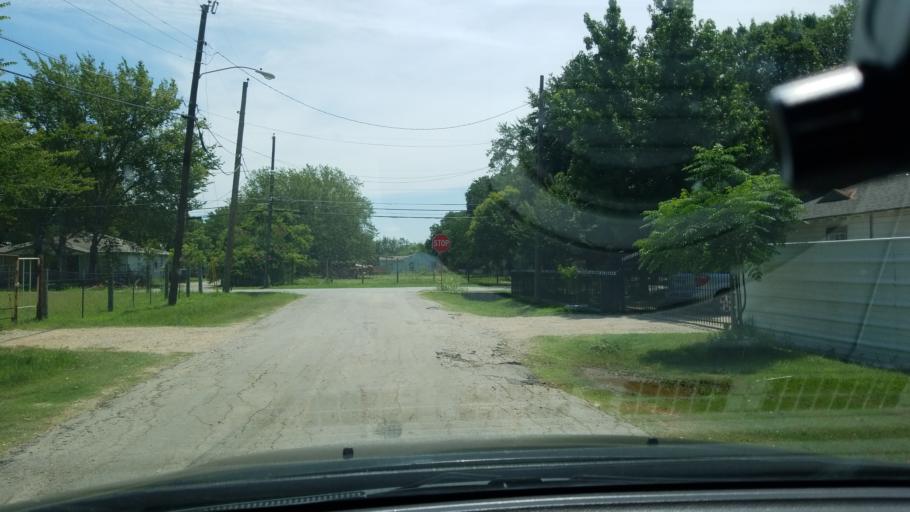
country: US
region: Texas
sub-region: Dallas County
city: Balch Springs
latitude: 32.7462
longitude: -96.6403
